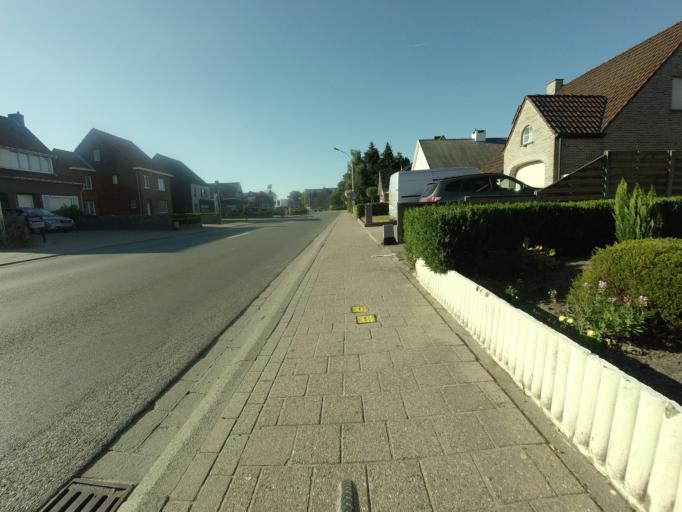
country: BE
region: Flanders
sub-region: Provincie Antwerpen
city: Beerse
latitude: 51.3229
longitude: 4.8340
